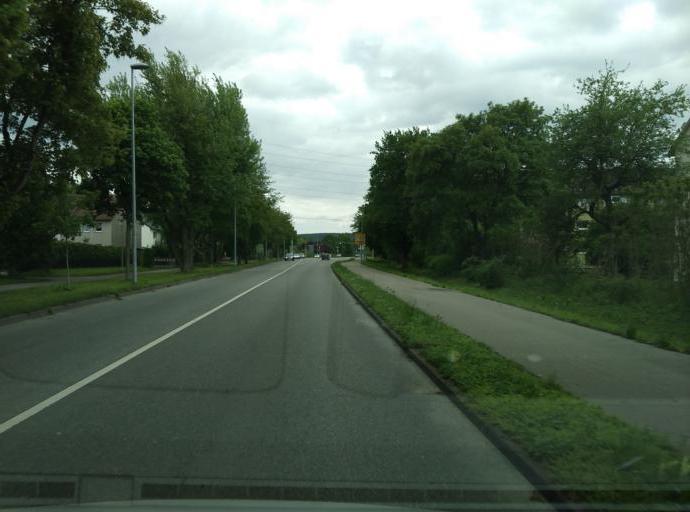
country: DE
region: Baden-Wuerttemberg
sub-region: Regierungsbezirk Stuttgart
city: Nurtingen
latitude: 48.6114
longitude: 9.3493
